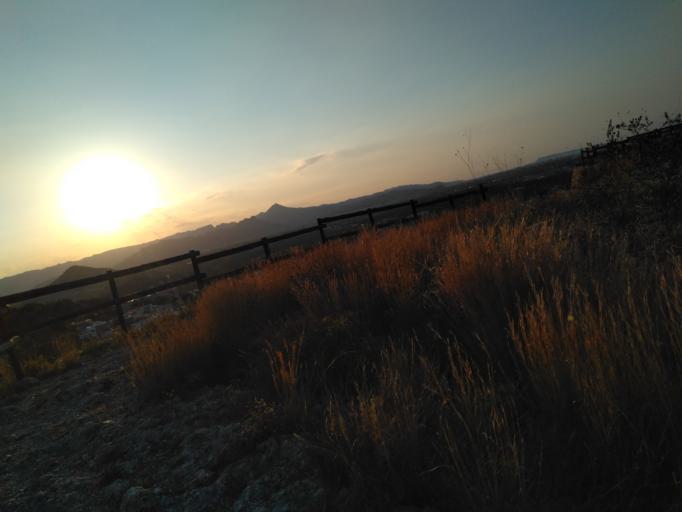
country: ES
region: Valencia
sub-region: Provincia de Valencia
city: Oliva
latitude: 38.9167
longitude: -0.1213
